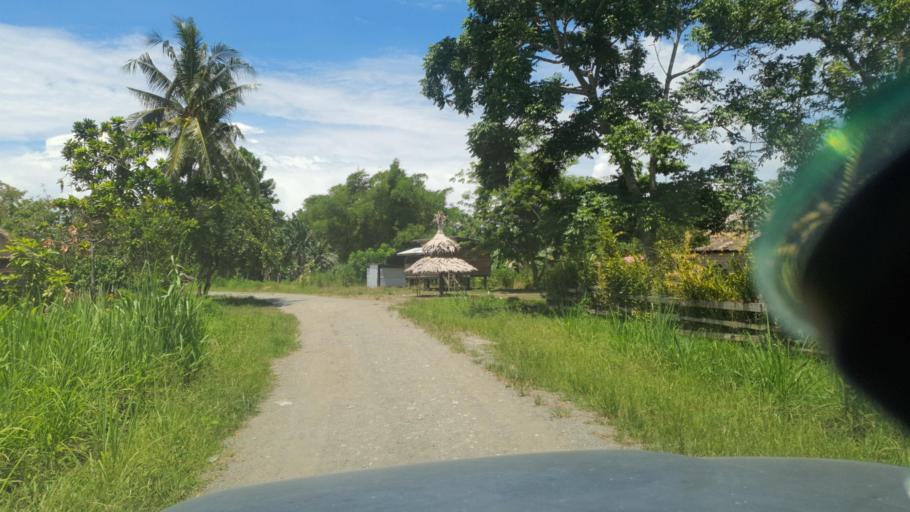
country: SB
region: Guadalcanal
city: Honiara
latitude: -9.4270
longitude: 160.1831
